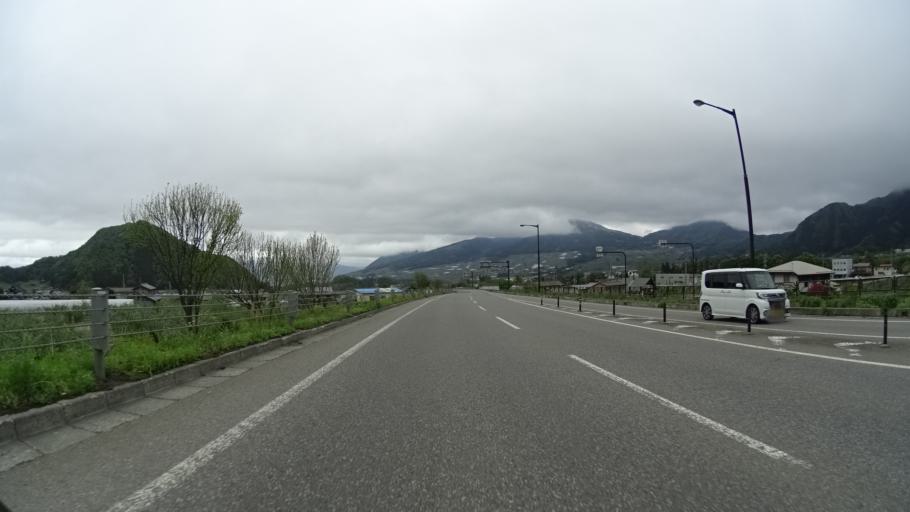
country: JP
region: Nagano
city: Nakano
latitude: 36.7439
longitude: 138.4034
